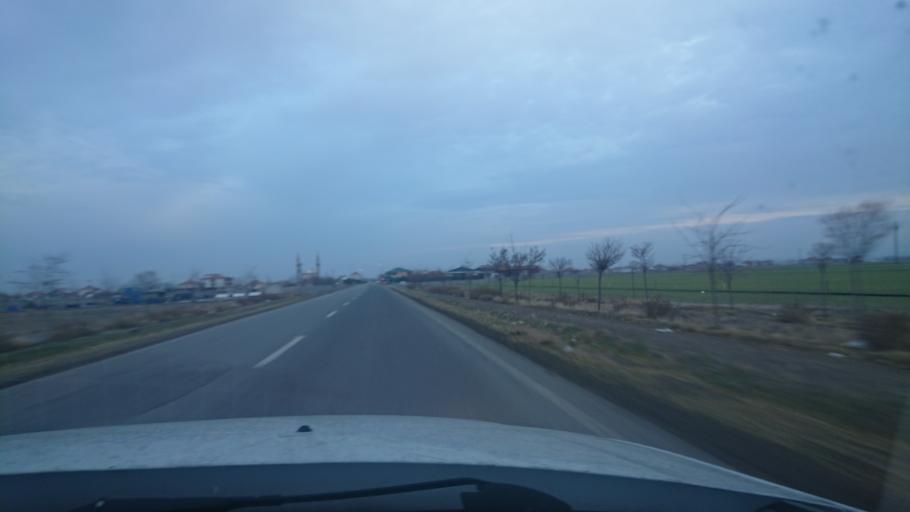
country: TR
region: Aksaray
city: Yesilova
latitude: 38.3294
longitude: 33.7525
